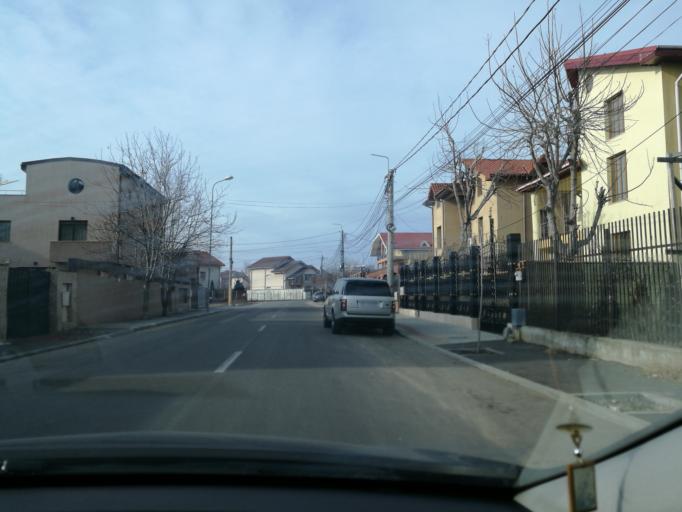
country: RO
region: Constanta
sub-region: Municipiul Constanta
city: Constanta
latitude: 44.1804
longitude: 28.6129
